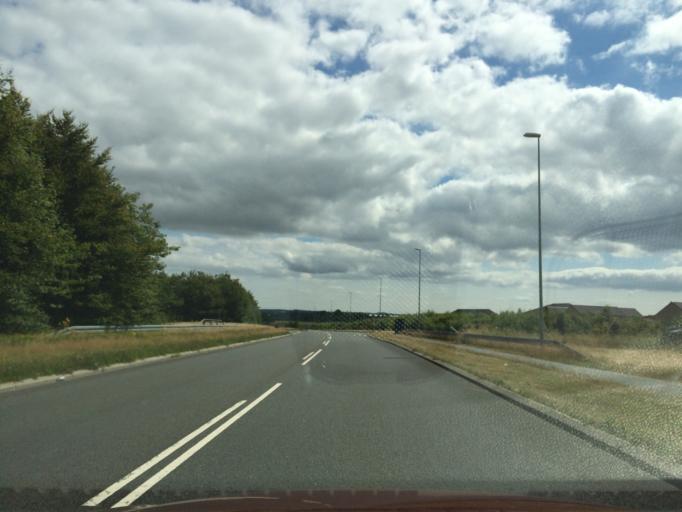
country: DK
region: Central Jutland
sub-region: Silkeborg Kommune
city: Svejbaek
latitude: 56.1897
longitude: 9.6117
